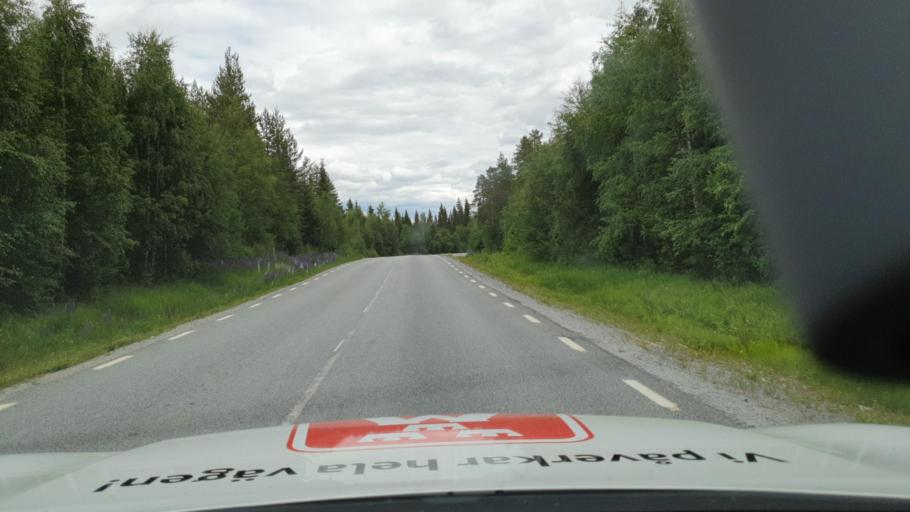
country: SE
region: Vaesterbotten
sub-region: Bjurholms Kommun
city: Bjurholm
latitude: 63.8833
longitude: 19.0436
